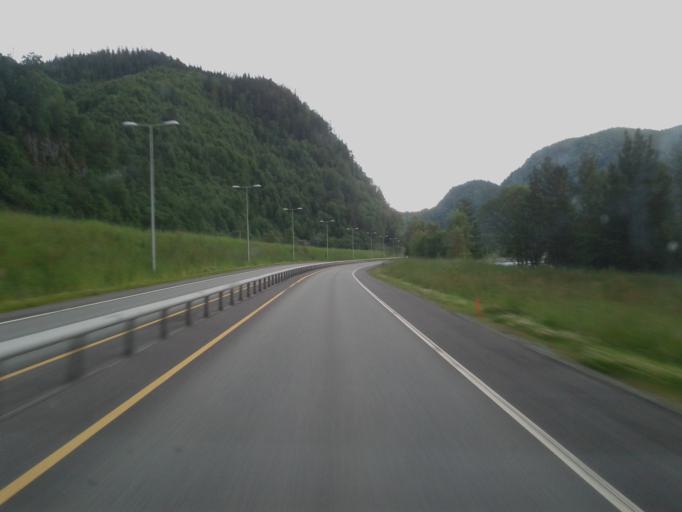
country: NO
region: Sor-Trondelag
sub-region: Midtre Gauldal
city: Storen
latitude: 63.0820
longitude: 10.2551
